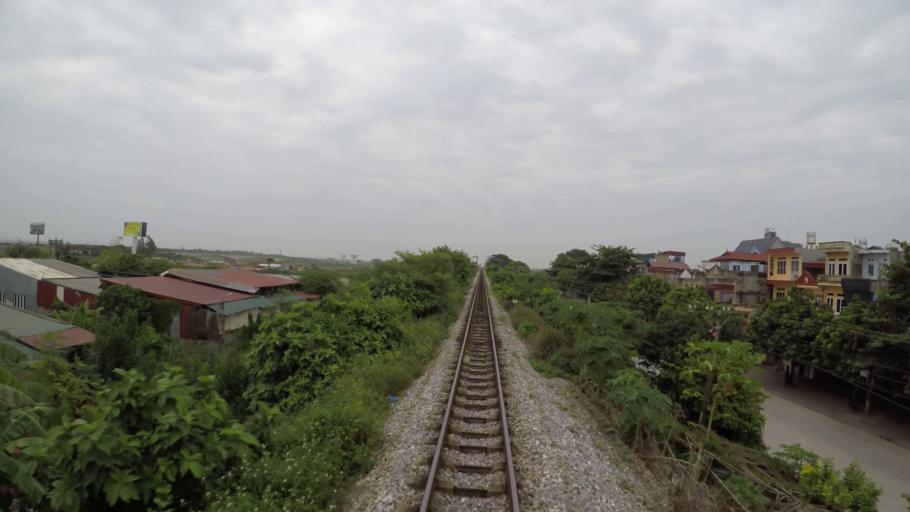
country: VN
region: Hai Duong
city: Thanh Pho Hai Duong
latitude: 20.9525
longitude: 106.3623
